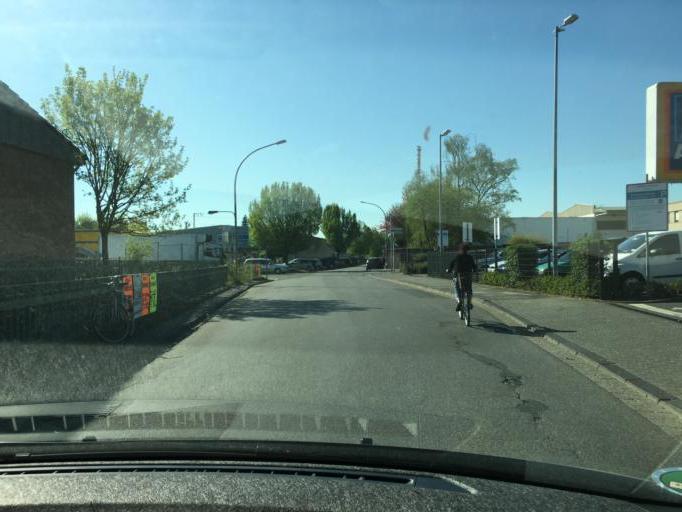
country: DE
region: North Rhine-Westphalia
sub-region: Regierungsbezirk Dusseldorf
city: Monchengladbach
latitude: 51.1627
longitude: 6.4385
